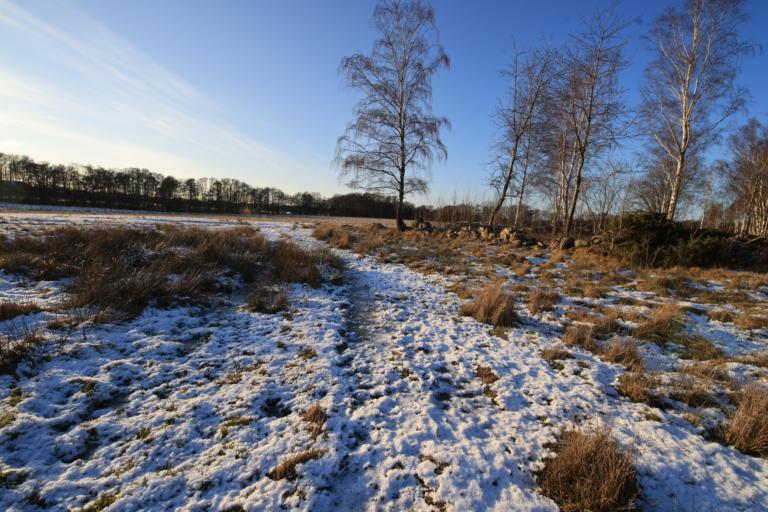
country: SE
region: Halland
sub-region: Varbergs Kommun
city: Varberg
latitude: 57.1292
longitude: 12.2991
